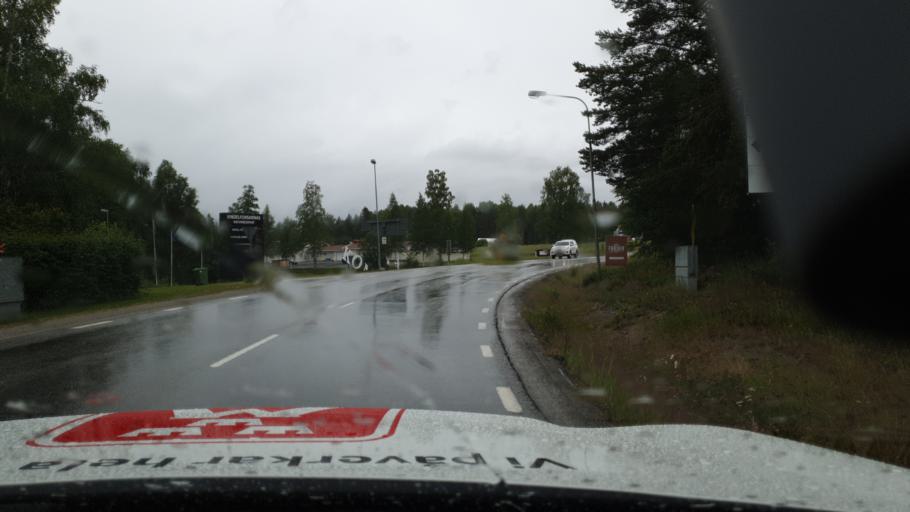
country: SE
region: Vaesterbotten
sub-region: Vindelns Kommun
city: Vindeln
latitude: 64.2114
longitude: 19.7158
